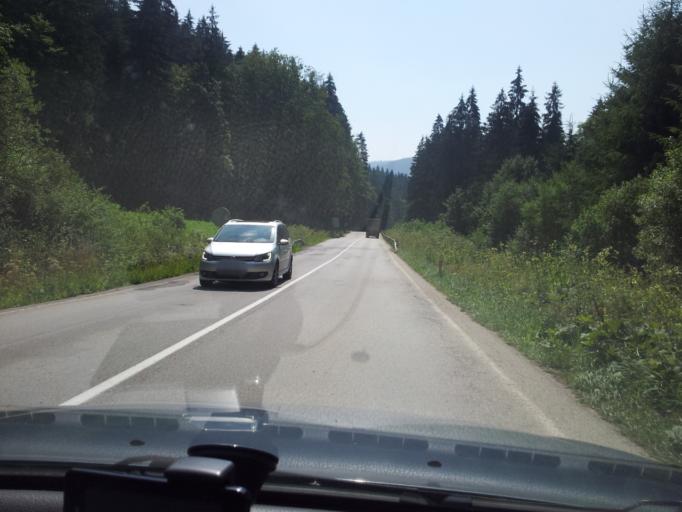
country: SK
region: Zilinsky
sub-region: Okres Dolny Kubin
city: Dolny Kubin
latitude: 49.2767
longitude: 19.3479
